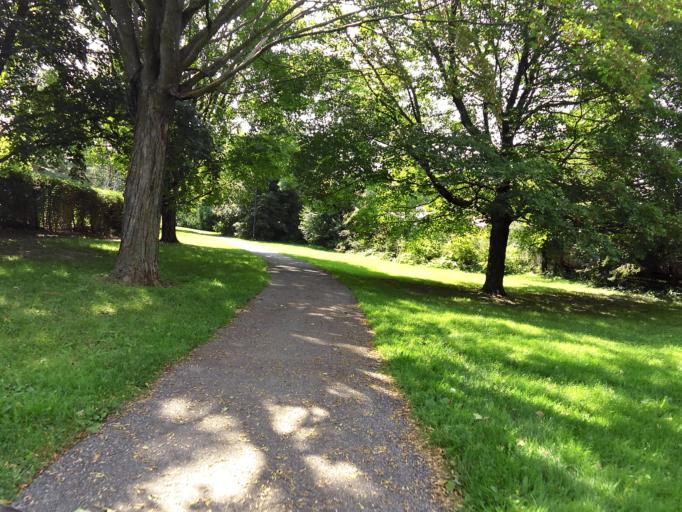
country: CA
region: Ontario
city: Bells Corners
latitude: 45.3298
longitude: -75.9077
